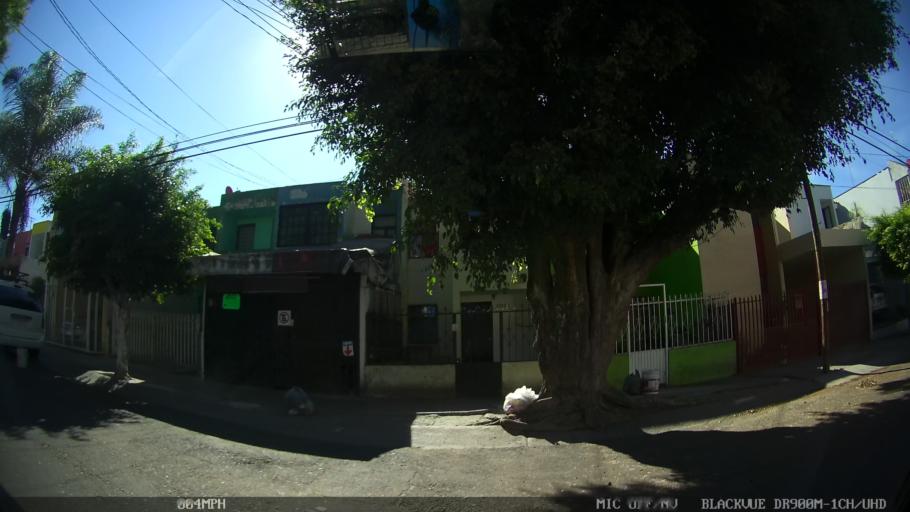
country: MX
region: Jalisco
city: Tlaquepaque
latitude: 20.6837
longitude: -103.2749
